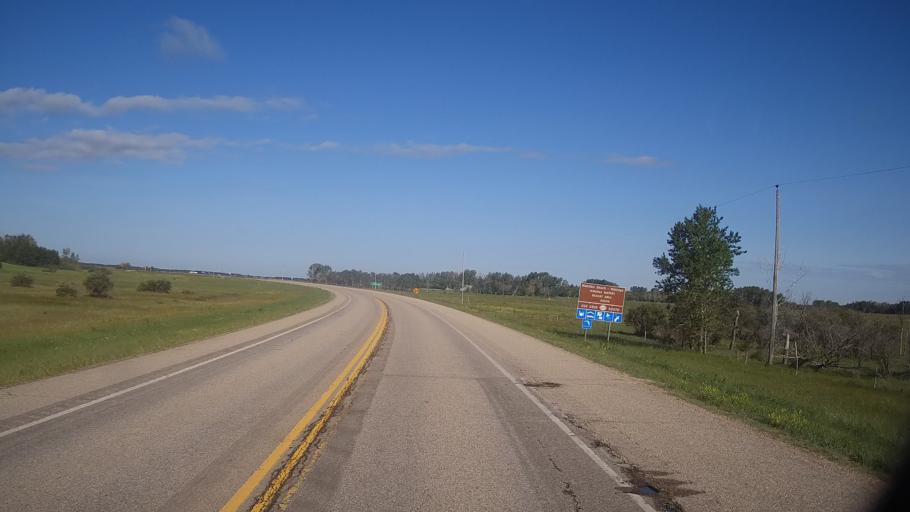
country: CA
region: Saskatchewan
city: Lanigan
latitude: 51.8747
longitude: -105.1840
